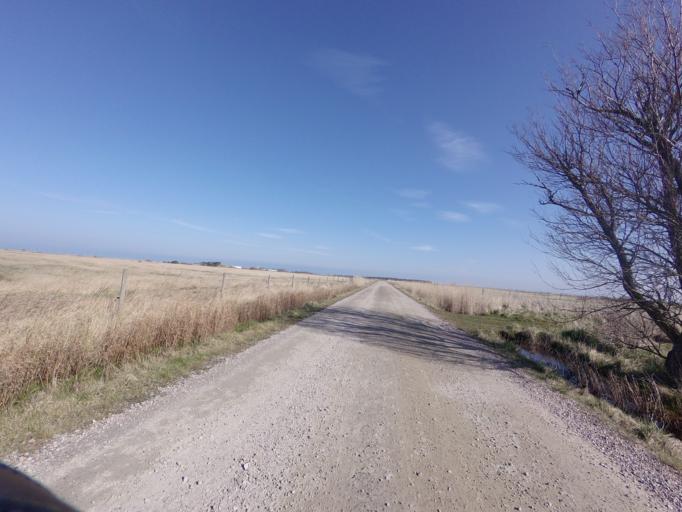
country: SE
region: Skane
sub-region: Vellinge Kommun
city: Skanor med Falsterbo
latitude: 55.4220
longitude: 12.8525
